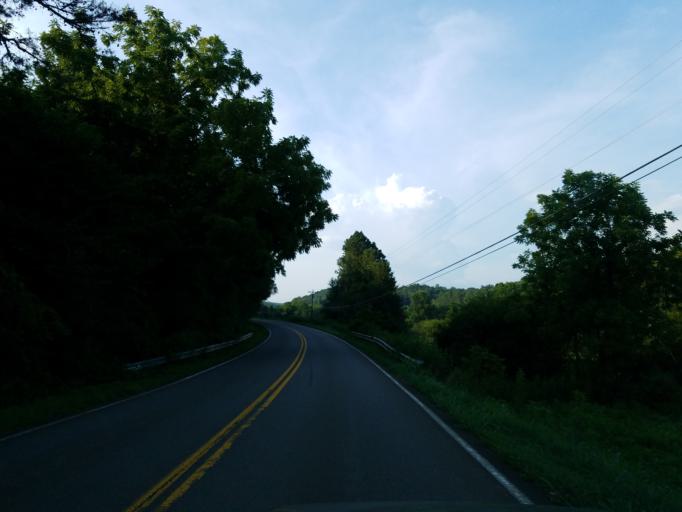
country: US
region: Georgia
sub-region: Gilmer County
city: Ellijay
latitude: 34.5699
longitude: -84.5357
